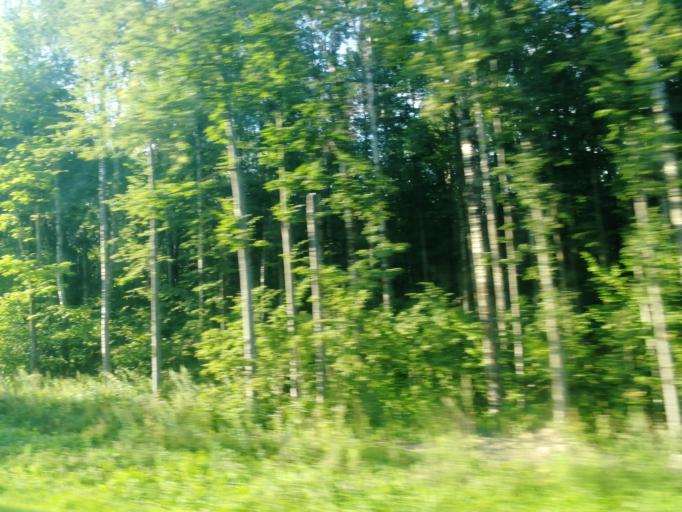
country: RU
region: Kaluga
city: Kaluga
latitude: 54.4456
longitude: 36.3158
